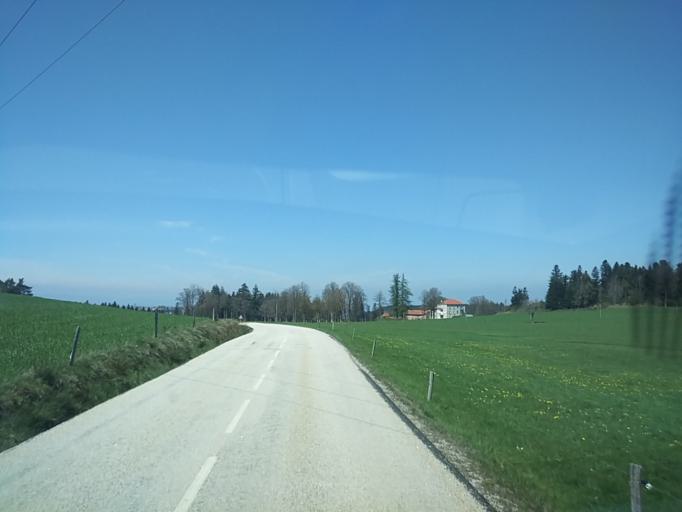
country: FR
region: Auvergne
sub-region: Departement de la Haute-Loire
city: Saint-Just-Malmont
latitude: 45.3237
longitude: 4.3335
